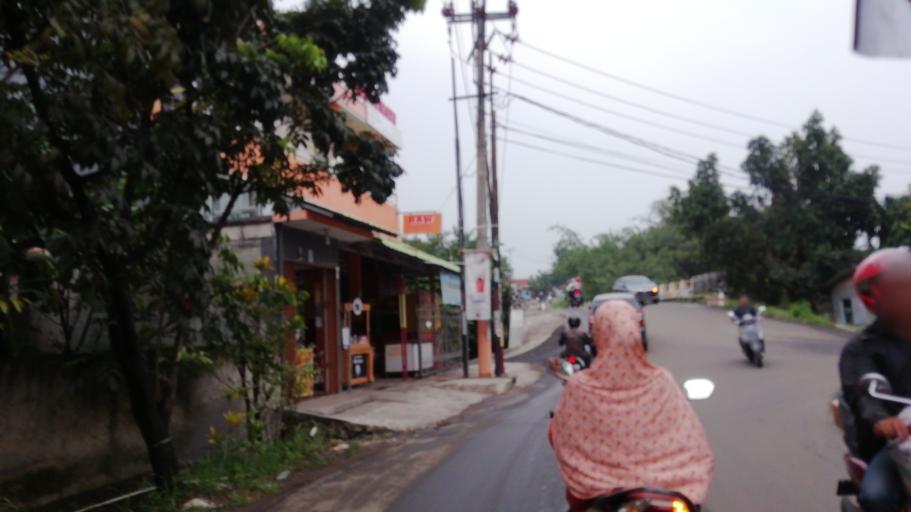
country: ID
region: West Java
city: Bogor
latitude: -6.5291
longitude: 106.8036
